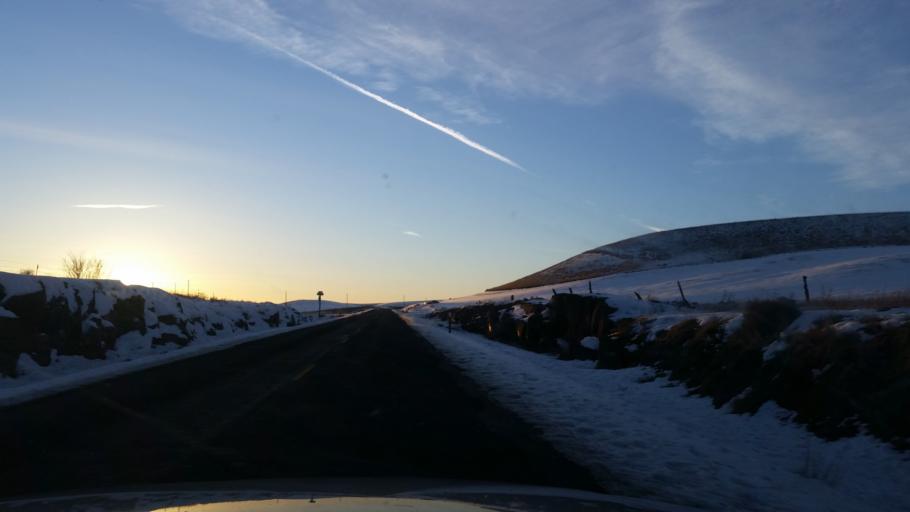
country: US
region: Washington
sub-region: Spokane County
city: Cheney
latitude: 47.1121
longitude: -117.8093
